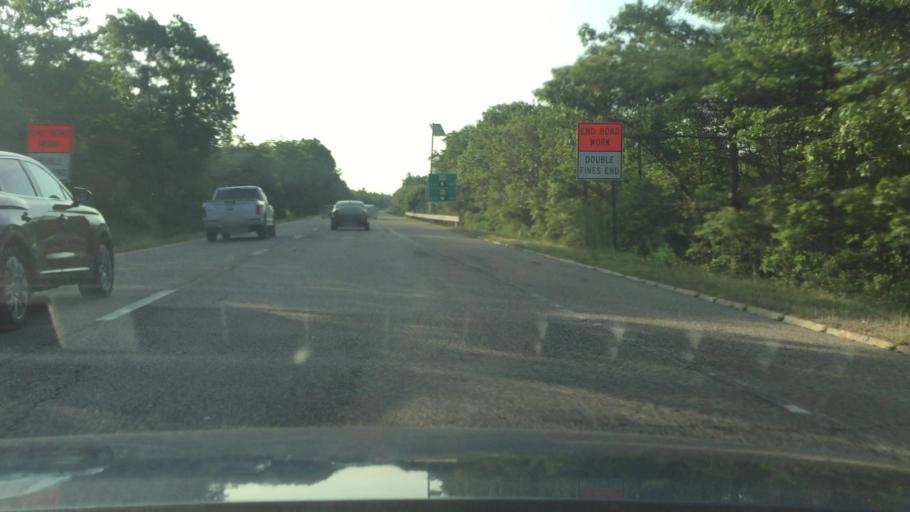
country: US
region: Massachusetts
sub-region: Plymouth County
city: Hanover
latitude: 42.1503
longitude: -70.8444
